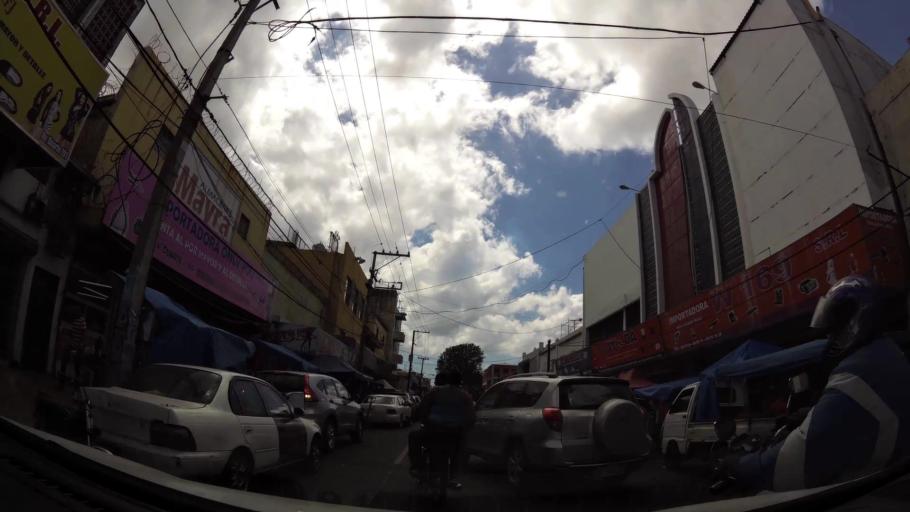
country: DO
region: Nacional
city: San Carlos
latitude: 18.4876
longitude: -69.8949
